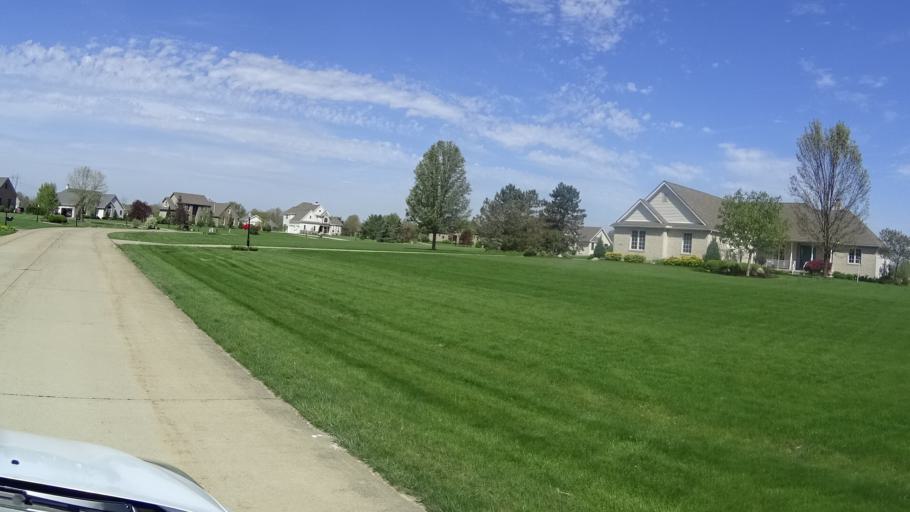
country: US
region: Ohio
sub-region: Lorain County
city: Lagrange
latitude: 41.2949
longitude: -82.1307
